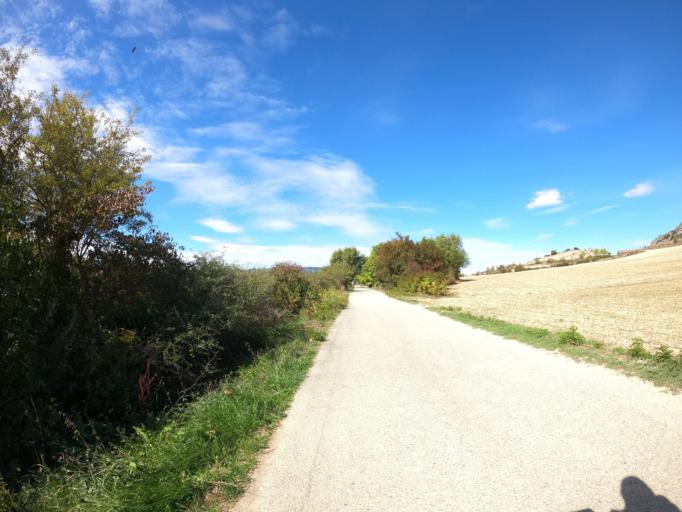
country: ES
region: Navarre
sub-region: Provincia de Navarra
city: Lumbier
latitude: 42.6368
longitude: -1.3061
